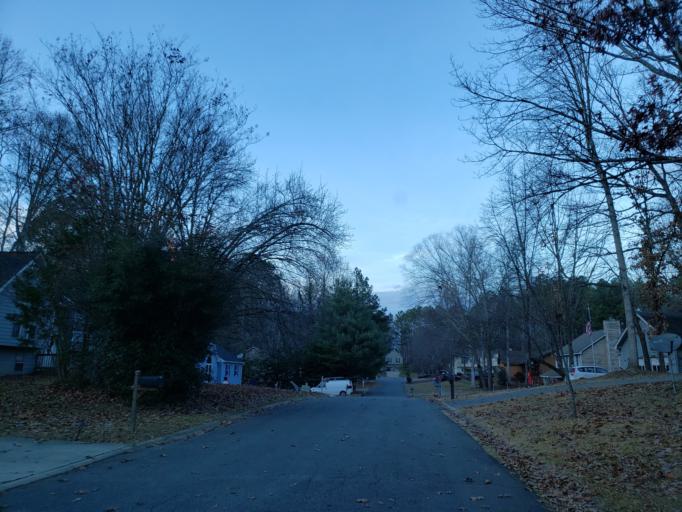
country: US
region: Georgia
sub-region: Cobb County
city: Acworth
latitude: 34.0445
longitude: -84.6504
